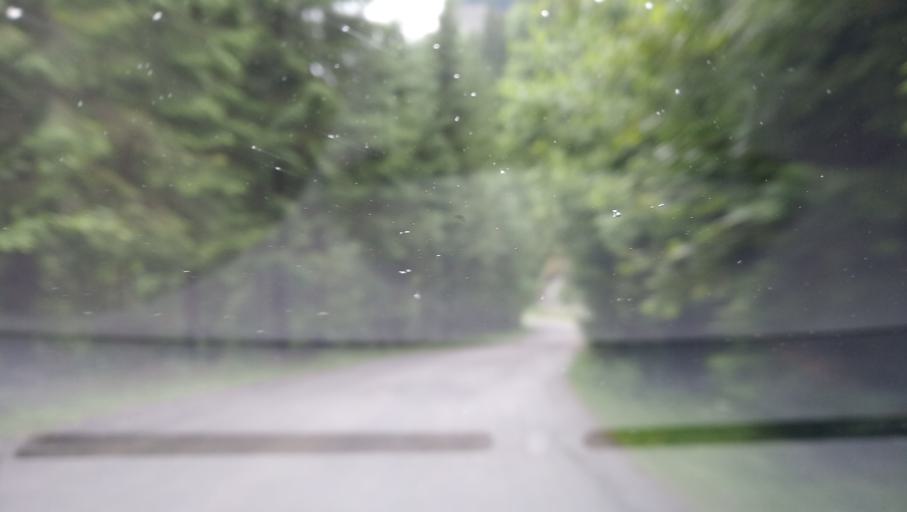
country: RO
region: Hunedoara
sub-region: Oras Petrila
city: Petrila
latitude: 45.4080
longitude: 23.5184
